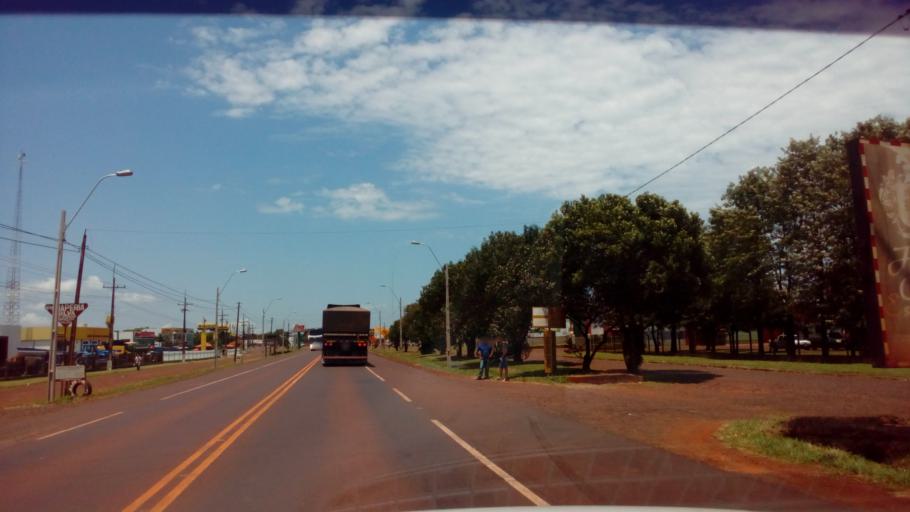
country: PY
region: Alto Parana
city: Santa Rita
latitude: -25.8188
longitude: -55.1109
